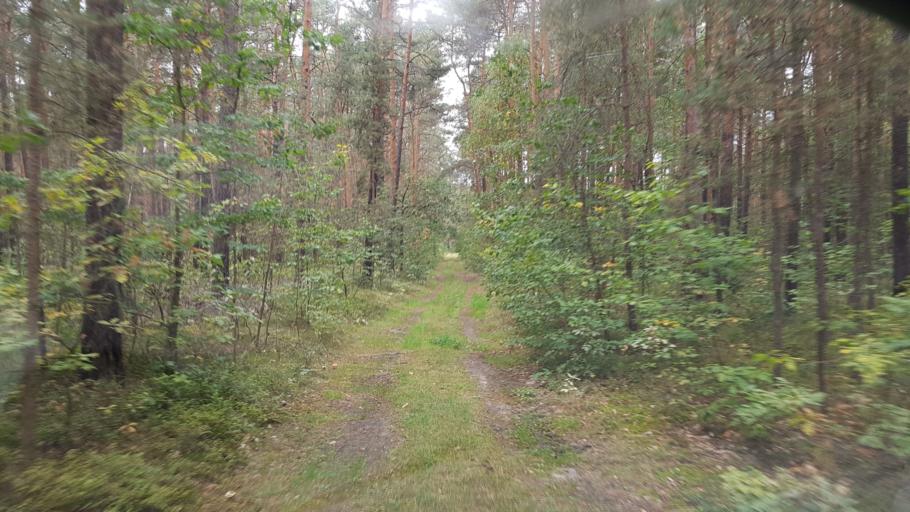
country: DE
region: Brandenburg
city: Finsterwalde
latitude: 51.5796
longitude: 13.6688
